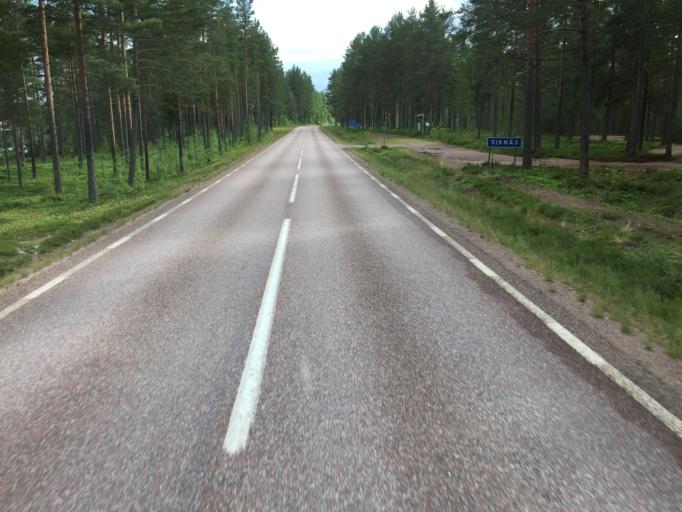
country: SE
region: Dalarna
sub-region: Vansbro Kommun
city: Vansbro
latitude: 60.7845
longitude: 14.1553
